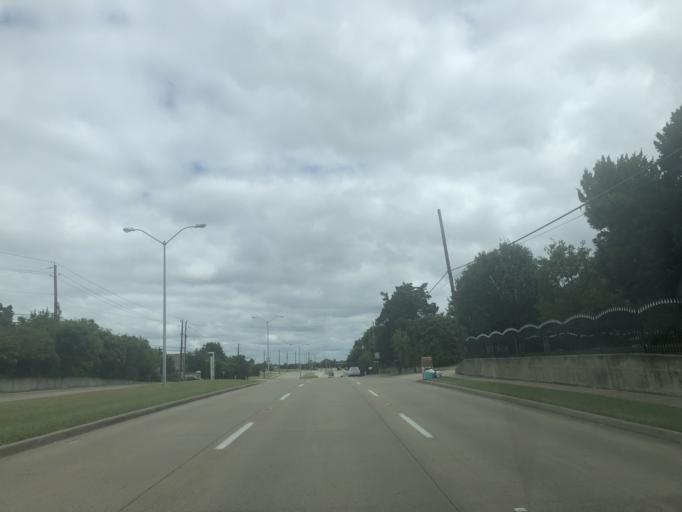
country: US
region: Texas
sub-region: Dallas County
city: Duncanville
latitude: 32.6581
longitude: -96.9430
